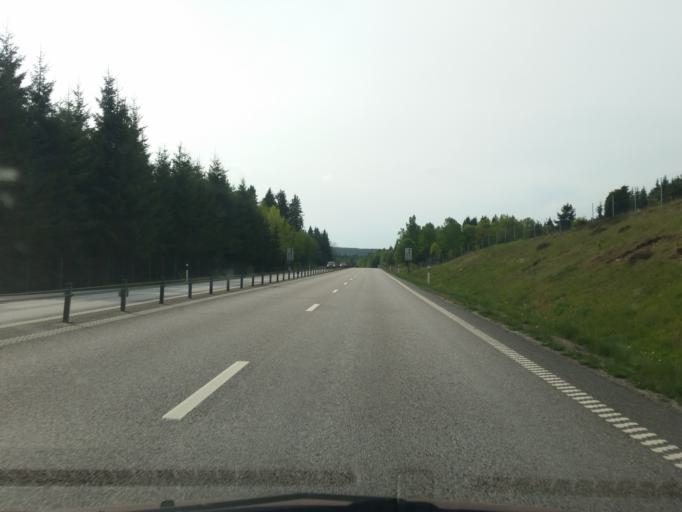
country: SE
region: Vaestra Goetaland
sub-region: Ulricehamns Kommun
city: Ulricehamn
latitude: 57.8007
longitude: 13.3846
